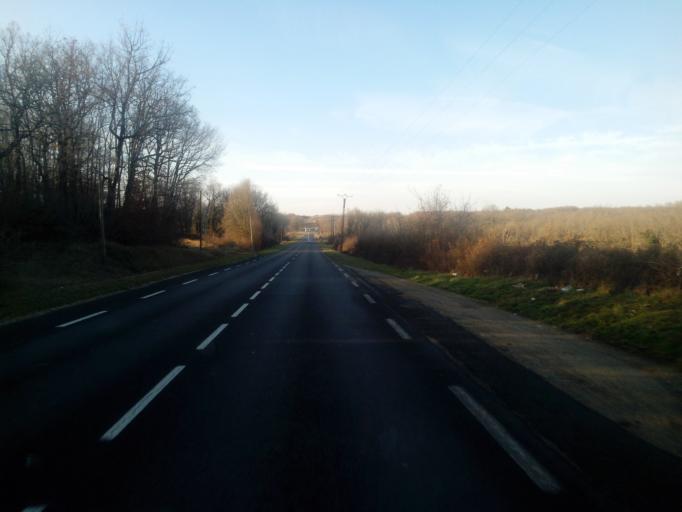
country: FR
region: Limousin
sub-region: Departement de la Correze
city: Brive-la-Gaillarde
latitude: 45.0283
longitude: 1.5143
